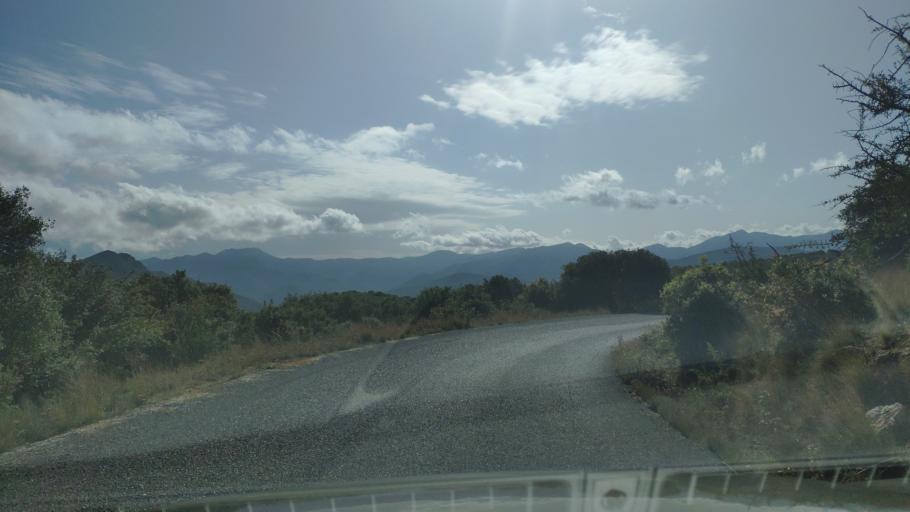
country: GR
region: Peloponnese
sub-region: Nomos Arkadias
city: Dimitsana
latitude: 37.5639
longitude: 22.0034
